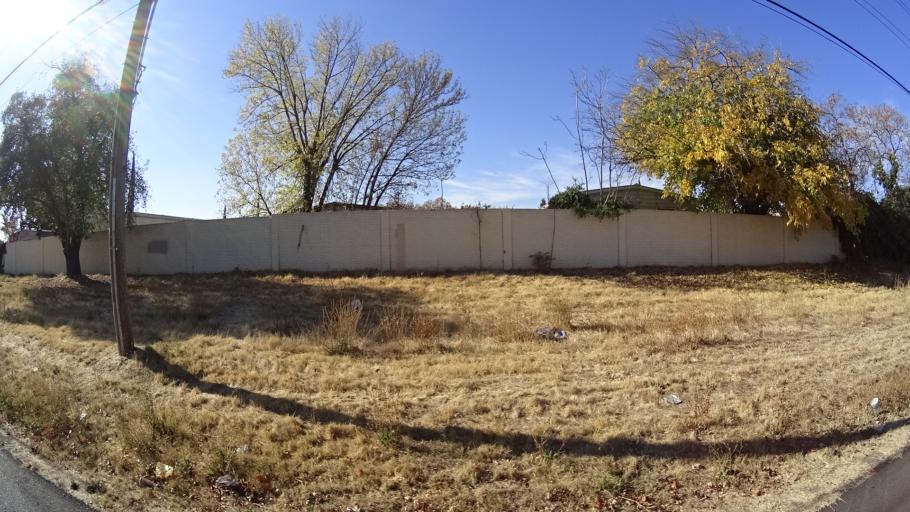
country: US
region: California
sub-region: Sacramento County
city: Antelope
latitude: 38.7026
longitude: -121.3263
